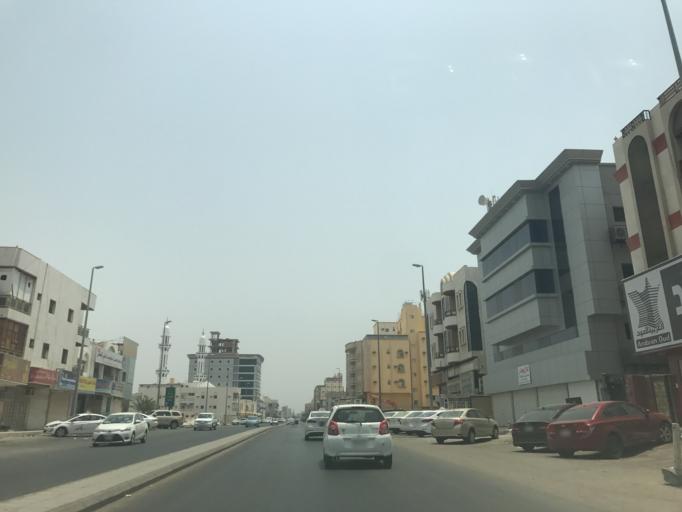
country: SA
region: Makkah
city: Jeddah
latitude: 21.5903
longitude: 39.1569
